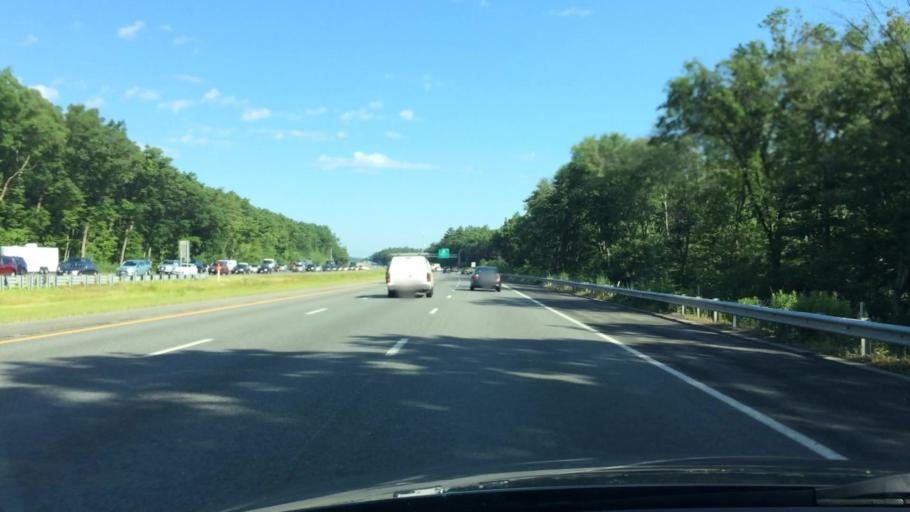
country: US
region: Massachusetts
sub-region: Middlesex County
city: Lexington
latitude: 42.4810
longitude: -71.2226
